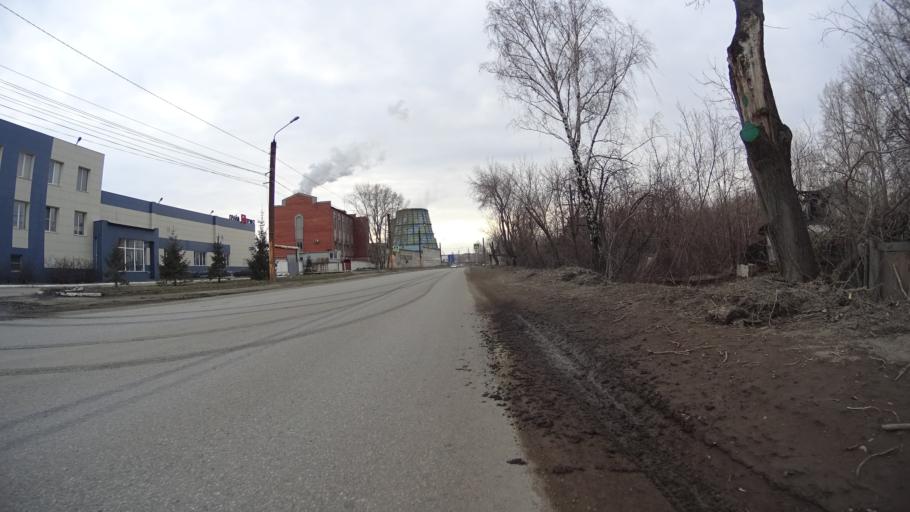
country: RU
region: Chelyabinsk
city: Zheleznodorozhnyy
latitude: 55.1564
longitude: 61.5060
